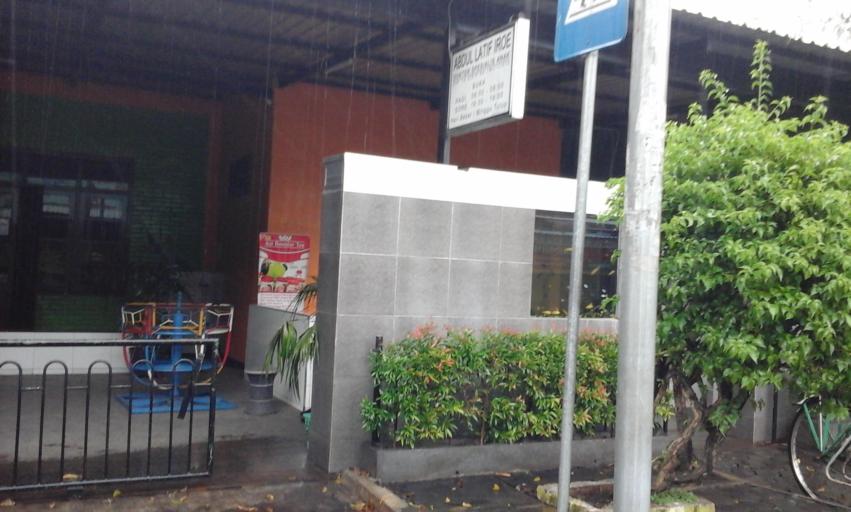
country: ID
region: East Java
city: Lumajang
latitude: -8.1370
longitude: 113.2248
